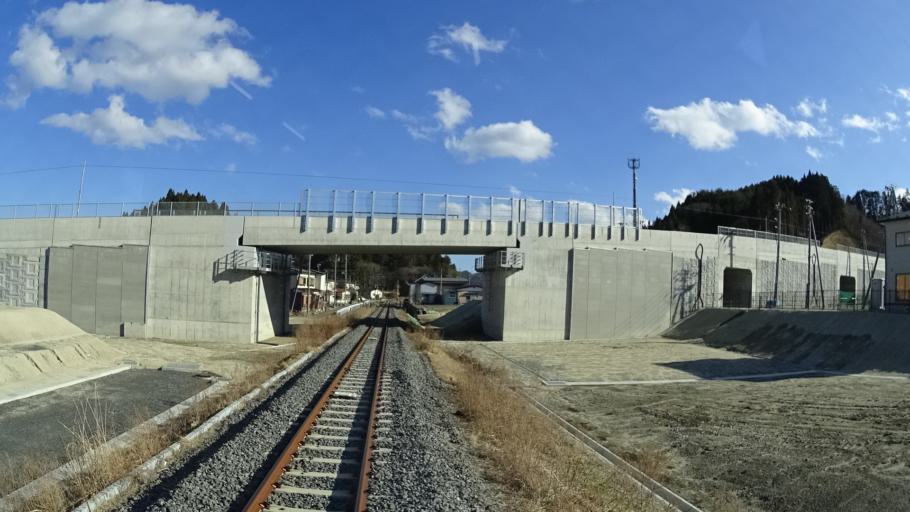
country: JP
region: Iwate
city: Yamada
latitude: 39.4732
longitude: 141.9479
